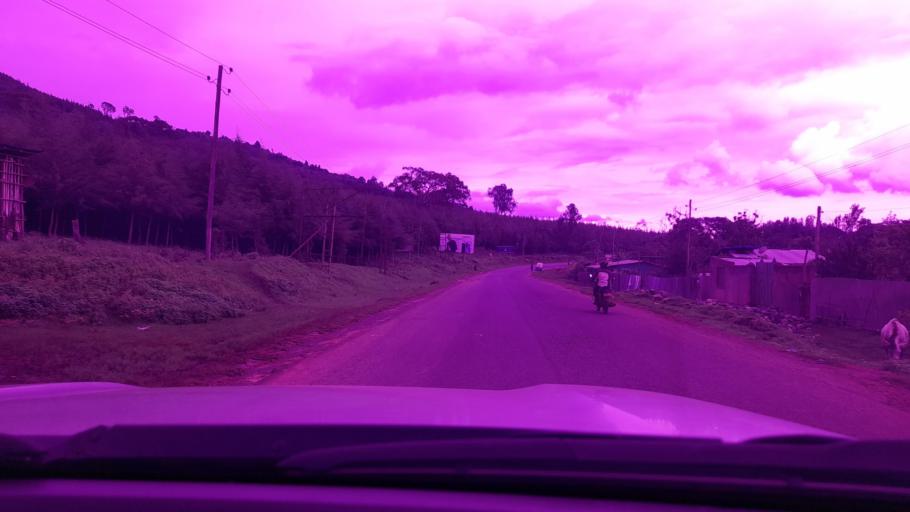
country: ET
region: Oromiya
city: Jima
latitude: 7.6683
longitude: 36.8709
